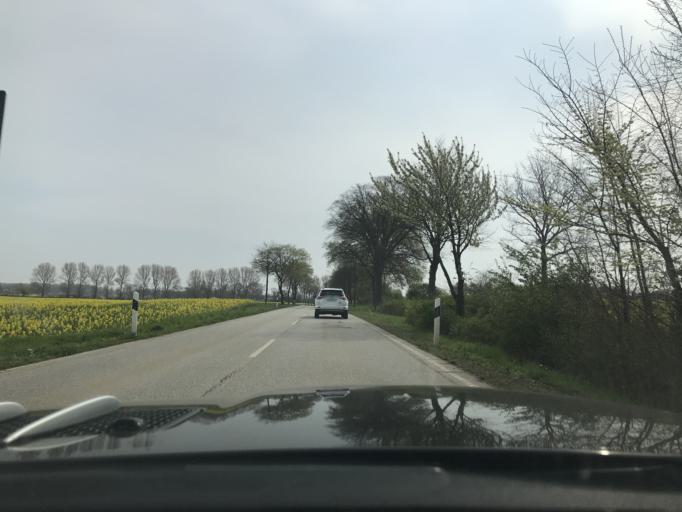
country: DE
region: Schleswig-Holstein
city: Heringsdorf
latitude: 54.2812
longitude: 11.0239
